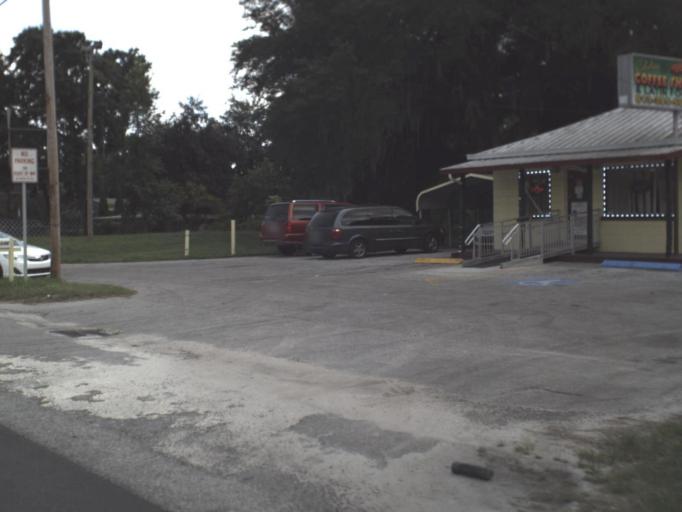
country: US
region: Florida
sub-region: Pasco County
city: Zephyrhills South
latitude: 28.2210
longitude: -82.1799
